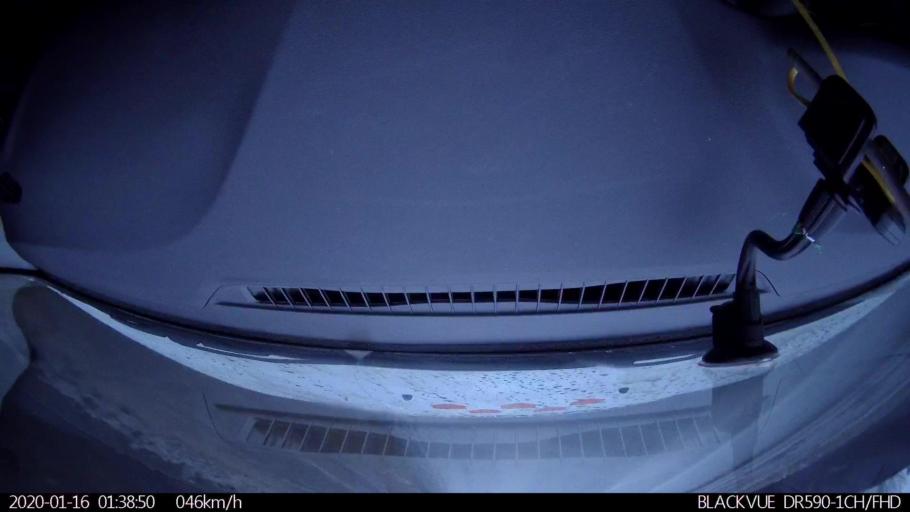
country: RU
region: Nizjnij Novgorod
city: Gorbatovka
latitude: 56.3373
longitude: 43.7988
